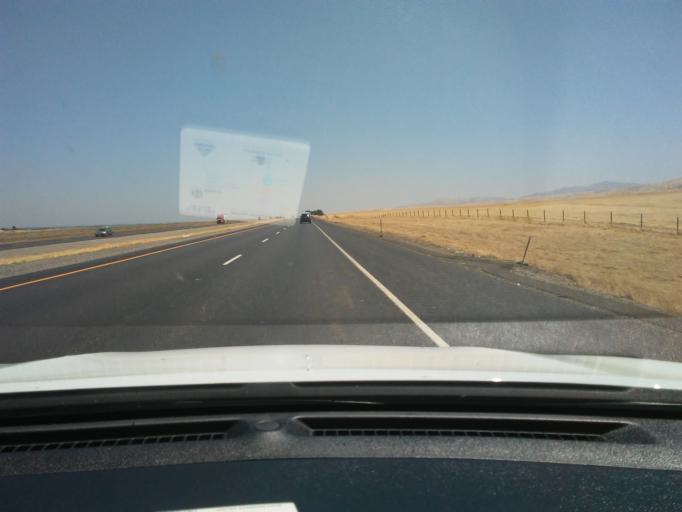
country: US
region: California
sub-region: San Joaquin County
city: Tracy
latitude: 37.6856
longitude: -121.4796
